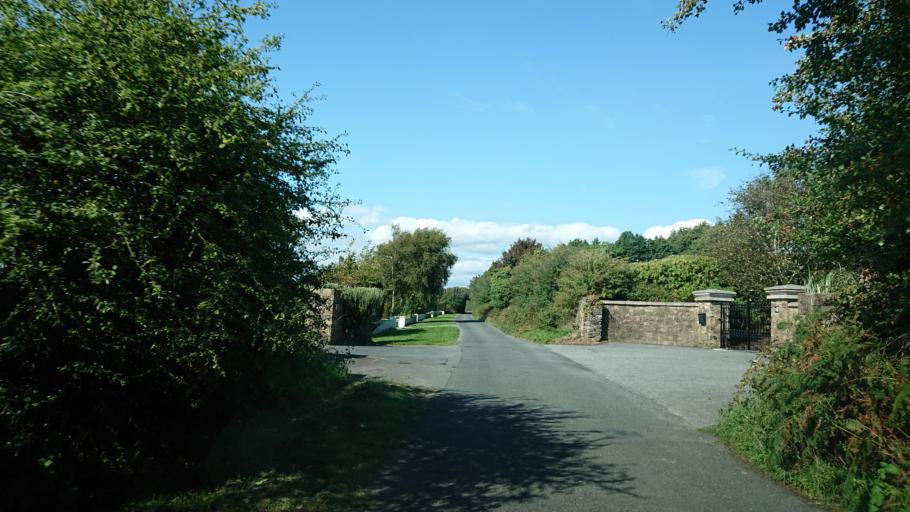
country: IE
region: Munster
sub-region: Waterford
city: Waterford
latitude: 52.2218
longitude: -7.0566
